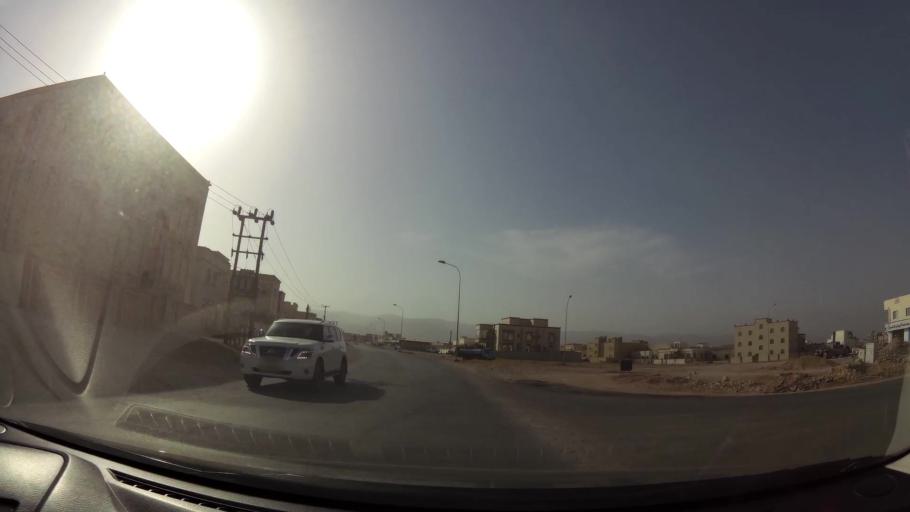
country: OM
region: Zufar
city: Salalah
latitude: 17.0091
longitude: 54.0198
